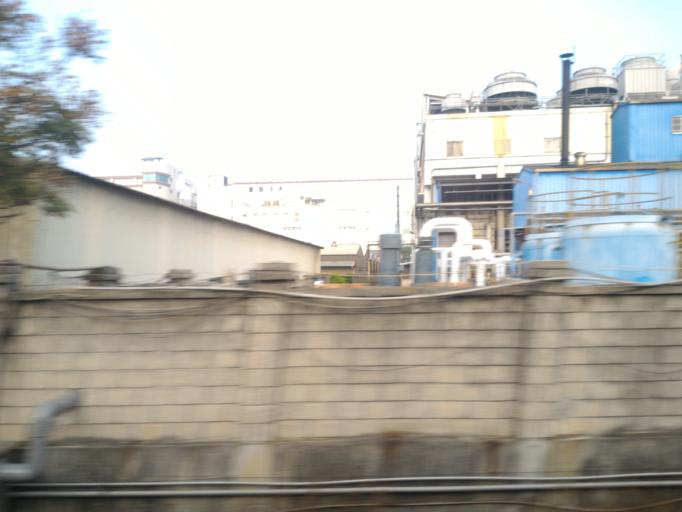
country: TW
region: Taiwan
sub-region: Taoyuan
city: Taoyuan
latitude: 24.9812
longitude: 121.3285
